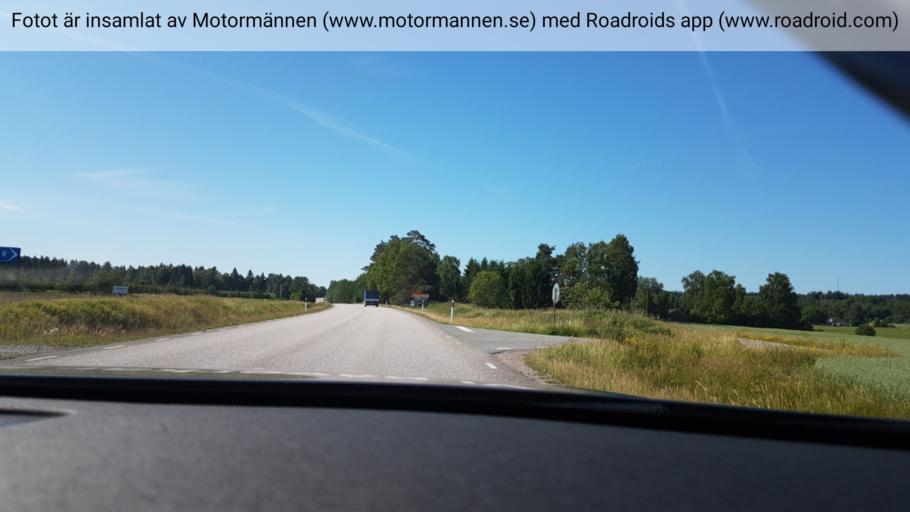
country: SE
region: Vaestra Goetaland
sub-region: Ulricehamns Kommun
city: Ulricehamn
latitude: 57.8705
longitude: 13.4318
